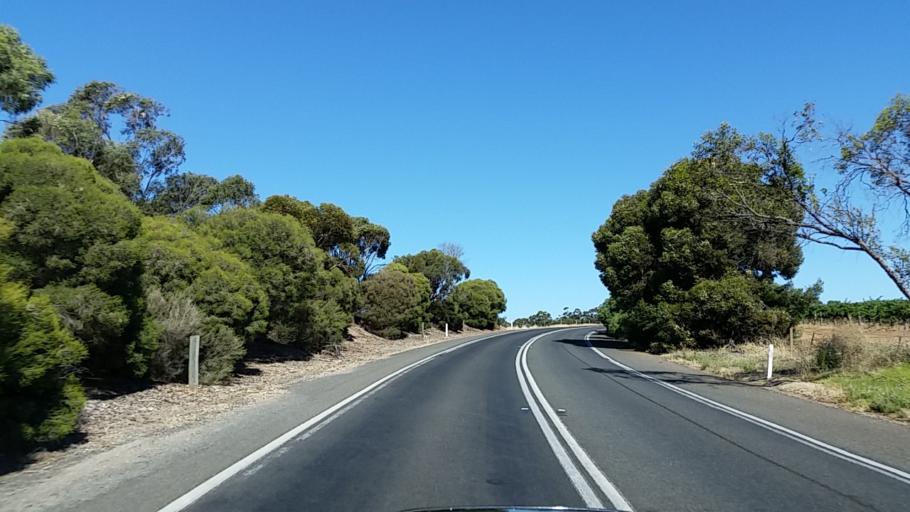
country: AU
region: South Australia
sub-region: Salisbury
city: Elizabeth
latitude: -34.7083
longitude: 138.7193
